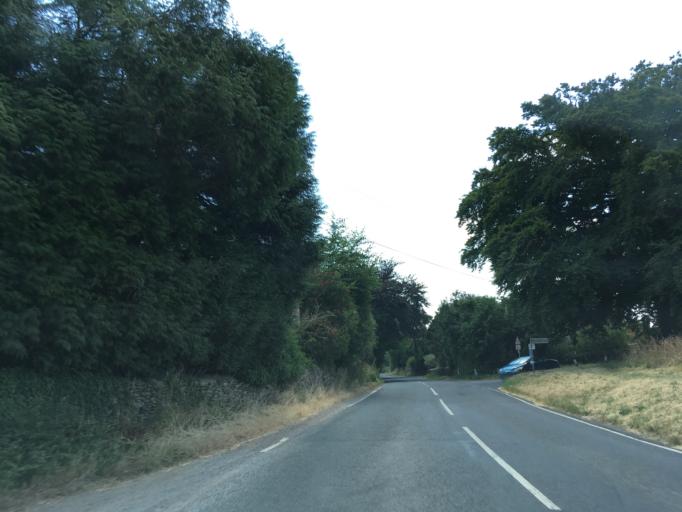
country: GB
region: England
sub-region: Gloucestershire
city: Stroud
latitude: 51.7721
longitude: -2.2355
